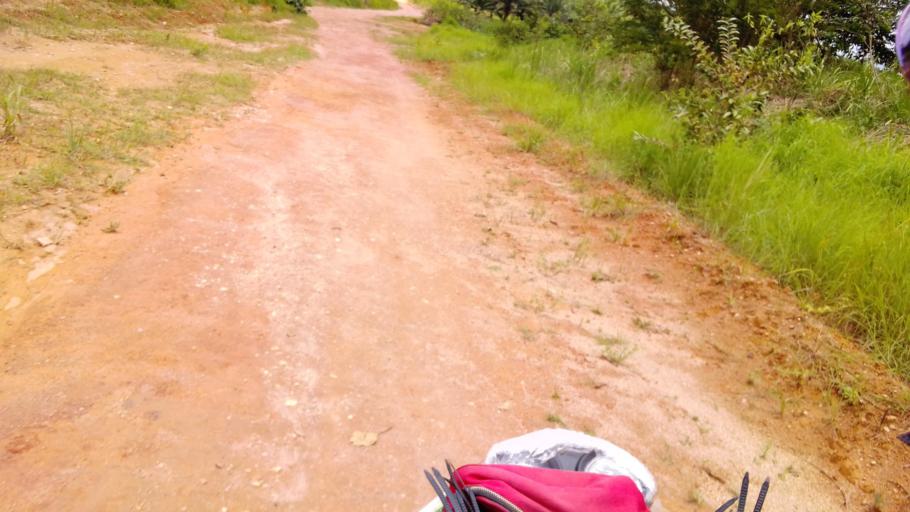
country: SL
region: Eastern Province
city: Koidu
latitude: 8.6783
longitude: -10.9551
